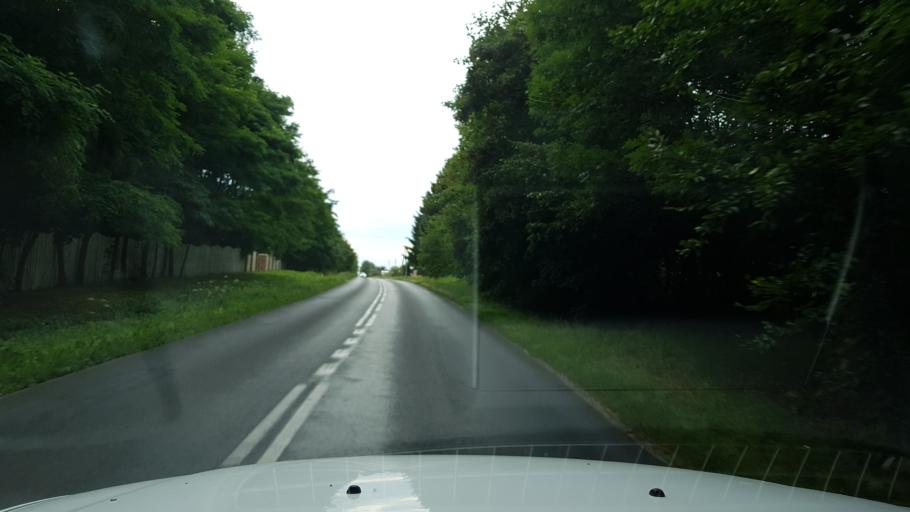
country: PL
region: West Pomeranian Voivodeship
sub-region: Powiat kolobrzeski
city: Dygowo
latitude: 54.1403
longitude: 15.7010
